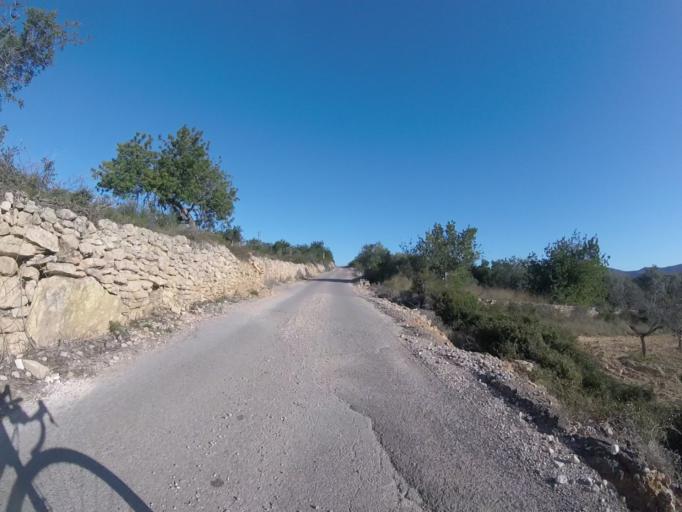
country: ES
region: Valencia
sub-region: Provincia de Castello
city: Alcala de Xivert
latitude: 40.2817
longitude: 0.2105
